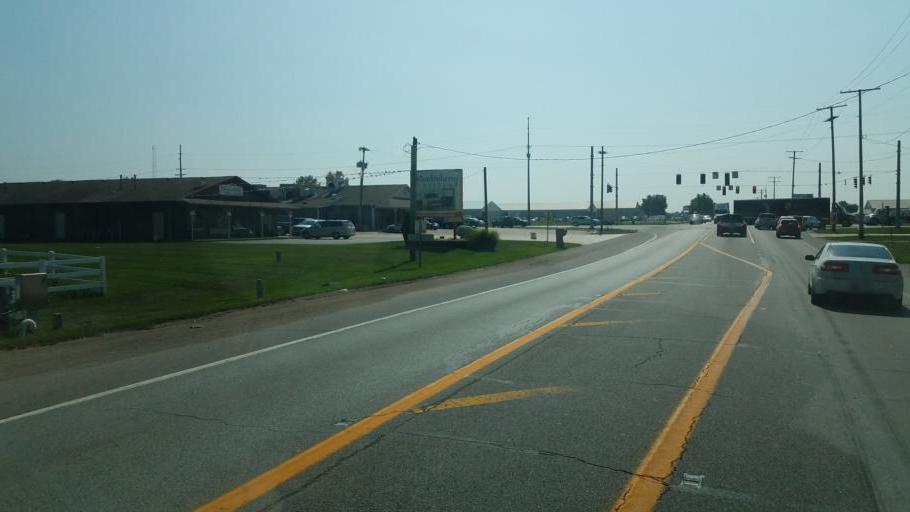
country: US
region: Indiana
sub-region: LaGrange County
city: Topeka
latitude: 41.6555
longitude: -85.5799
